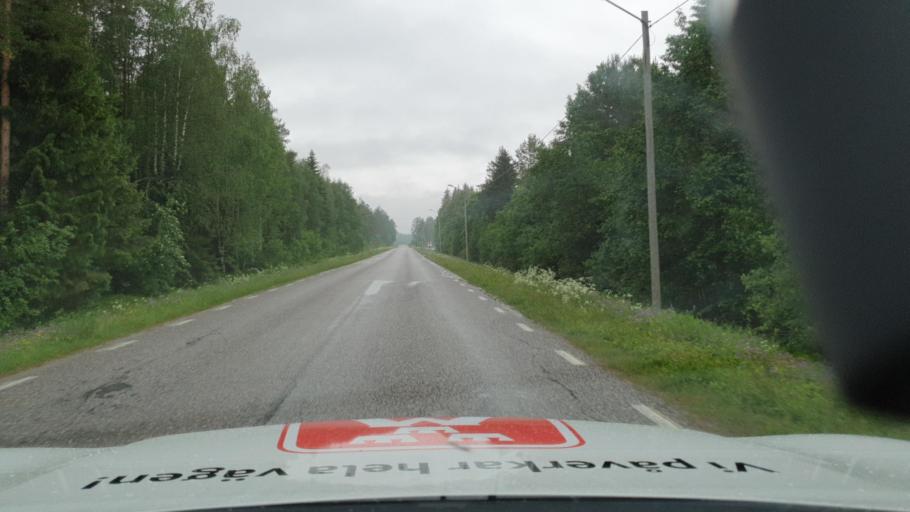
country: SE
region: Vaesterbotten
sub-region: Nordmalings Kommun
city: Nordmaling
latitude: 63.7926
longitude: 19.5416
